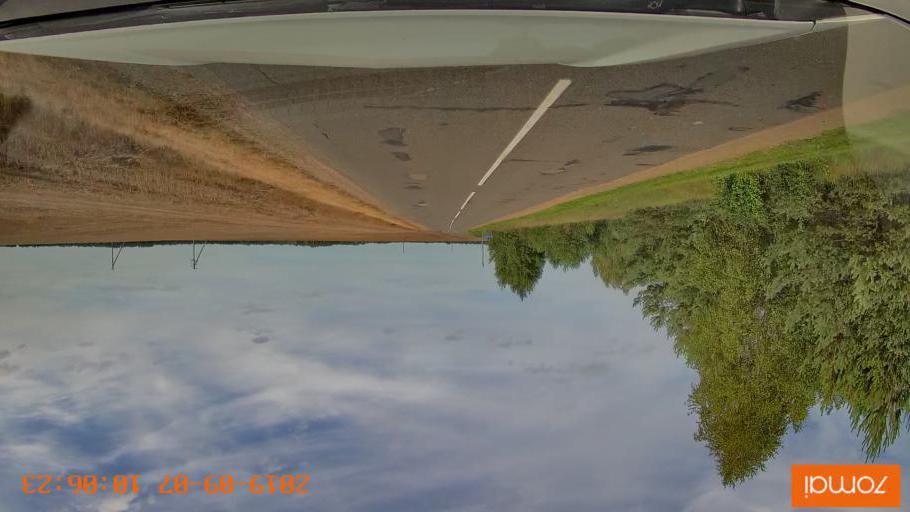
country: BY
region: Grodnenskaya
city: Voranava
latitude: 54.0612
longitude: 25.4032
